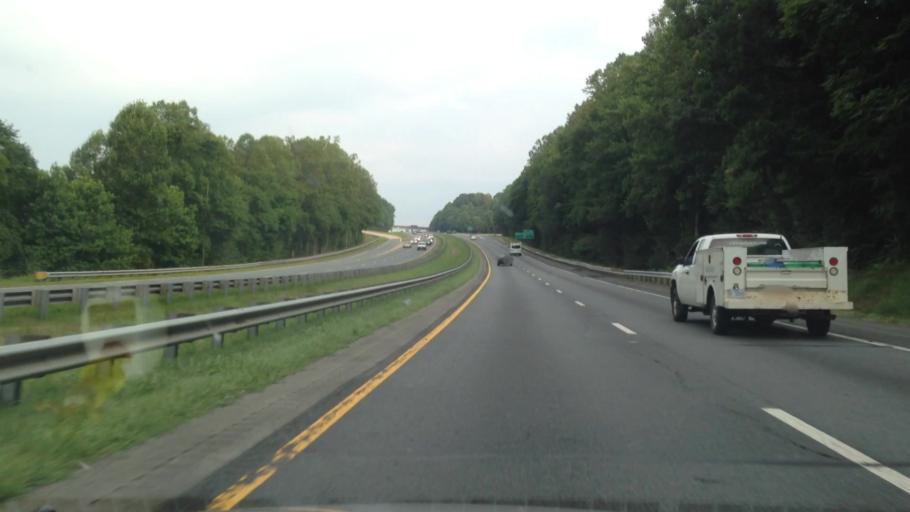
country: US
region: North Carolina
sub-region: Forsyth County
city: Rural Hall
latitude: 36.2245
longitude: -80.3166
